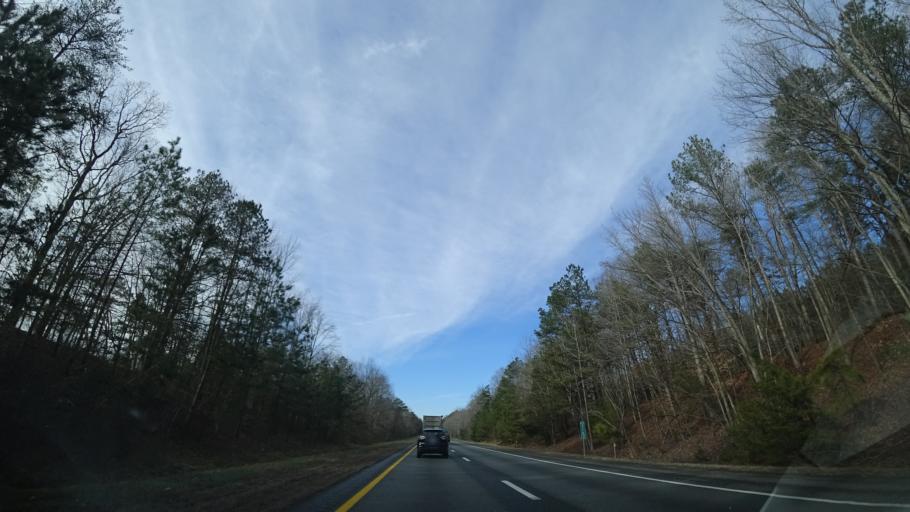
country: US
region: Virginia
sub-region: New Kent County
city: New Kent
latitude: 37.4900
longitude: -76.9933
